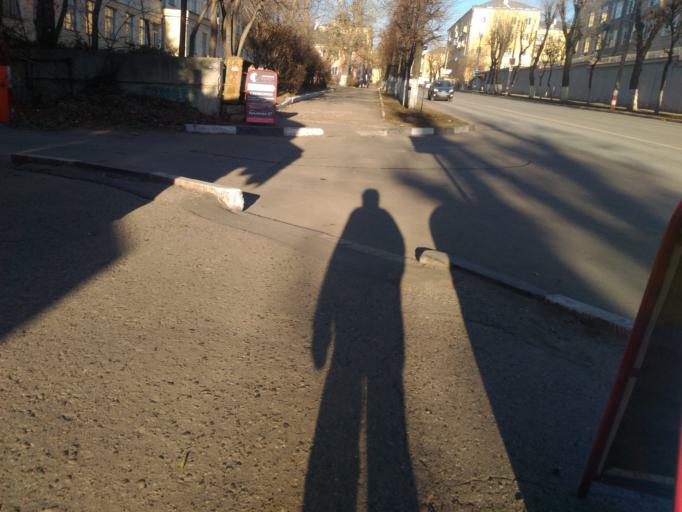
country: RU
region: Ulyanovsk
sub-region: Ulyanovskiy Rayon
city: Ulyanovsk
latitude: 54.3204
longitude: 48.3862
